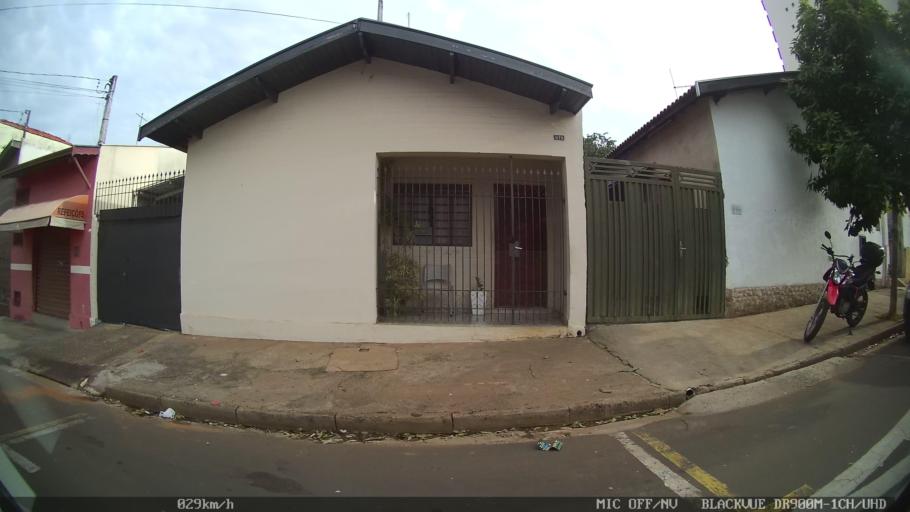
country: BR
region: Sao Paulo
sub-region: Piracicaba
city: Piracicaba
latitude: -22.7299
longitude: -47.6305
